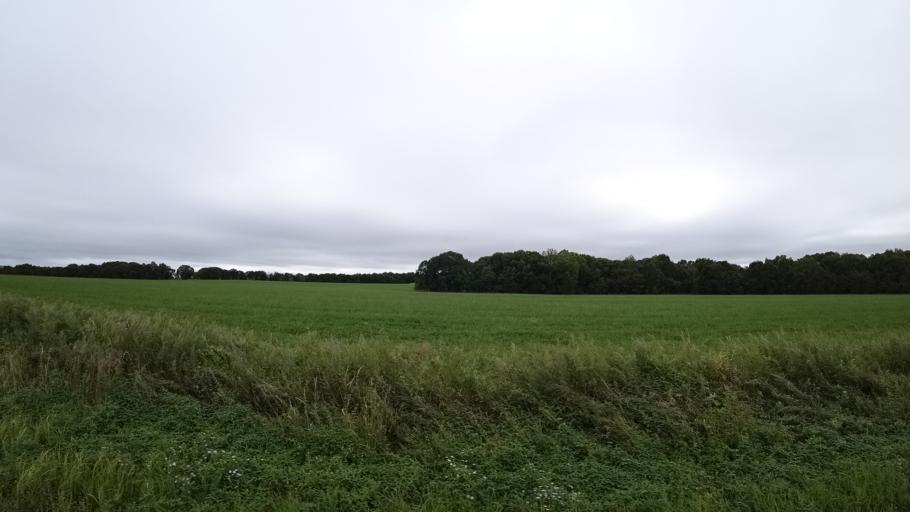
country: RU
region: Primorskiy
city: Rettikhovka
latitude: 44.0687
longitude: 132.6430
